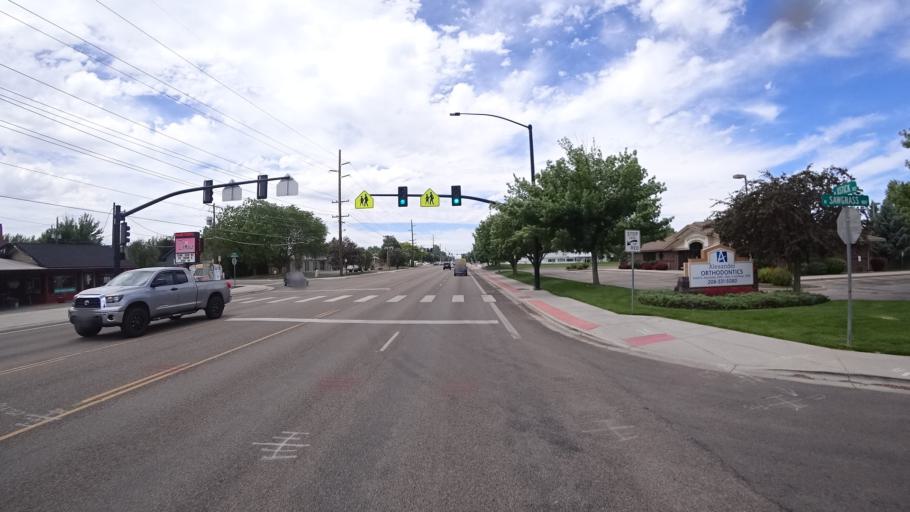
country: US
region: Idaho
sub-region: Ada County
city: Garden City
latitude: 43.6341
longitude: -116.2812
